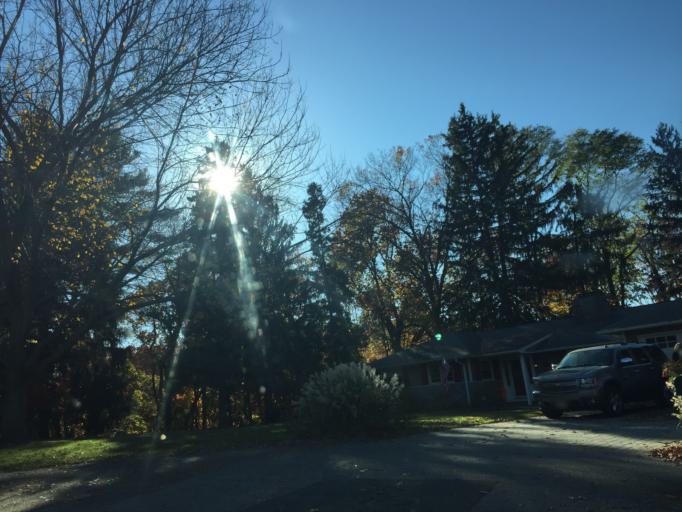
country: US
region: Maryland
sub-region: Baltimore County
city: Parkville
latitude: 39.4045
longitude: -76.5573
